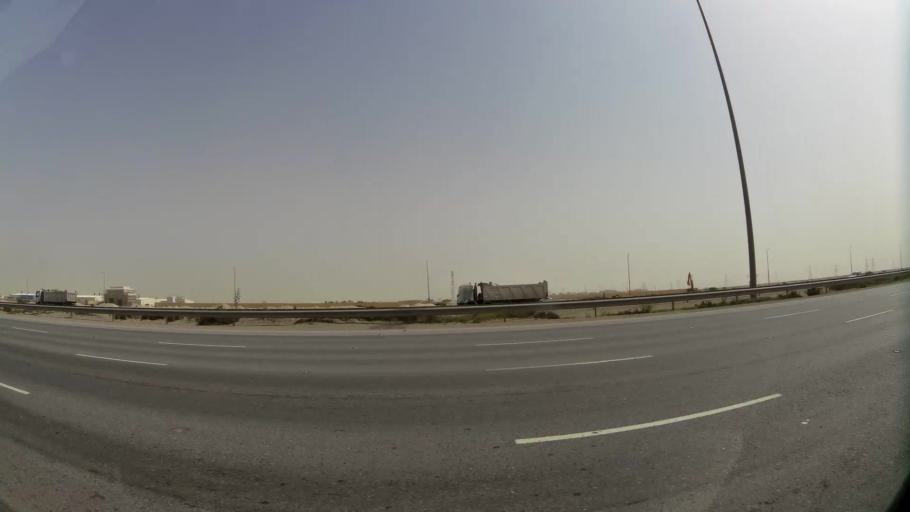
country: QA
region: Baladiyat ar Rayyan
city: Ar Rayyan
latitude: 25.1798
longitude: 51.3462
